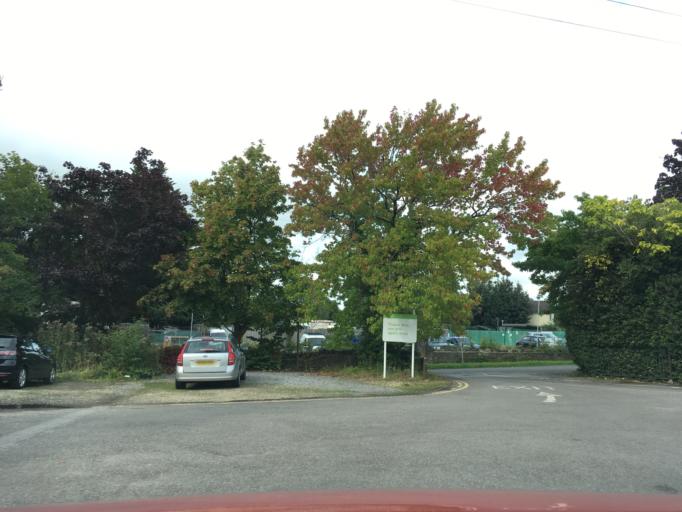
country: GB
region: England
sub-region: South Gloucestershire
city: Tytherington
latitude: 51.6079
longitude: -2.4884
